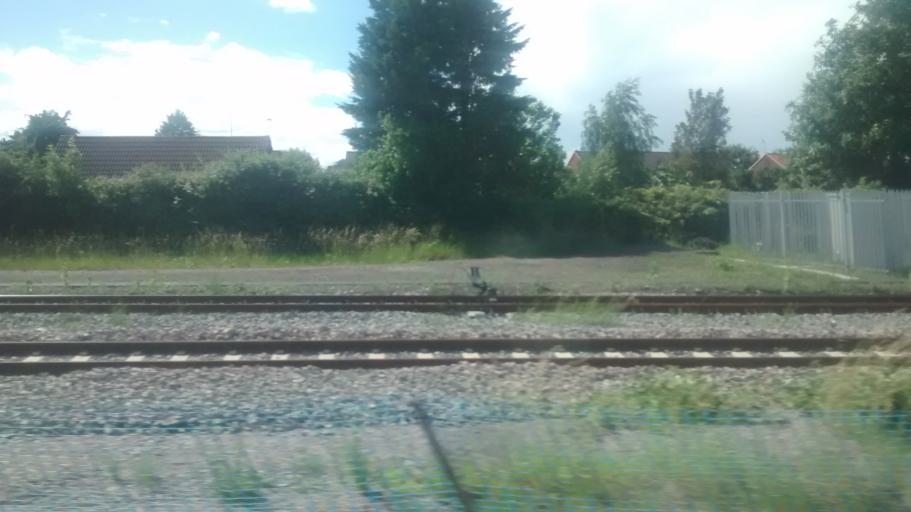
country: GB
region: England
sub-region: Cambridgeshire
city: Cambridge
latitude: 52.2225
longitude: 0.1576
